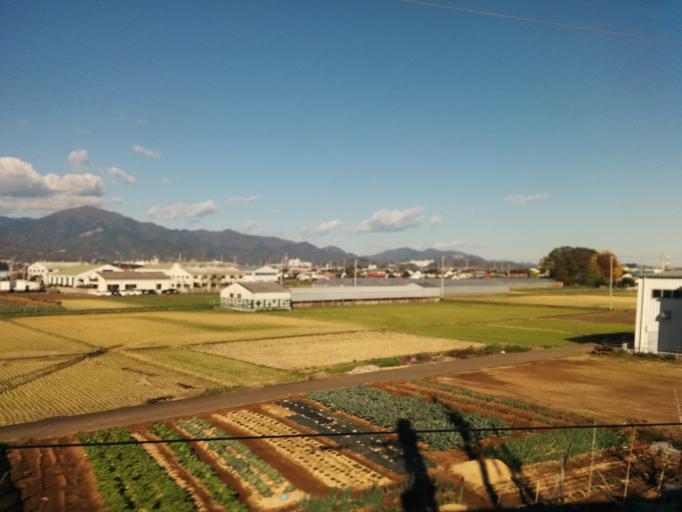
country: JP
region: Kanagawa
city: Isehara
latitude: 35.3733
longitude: 139.3448
